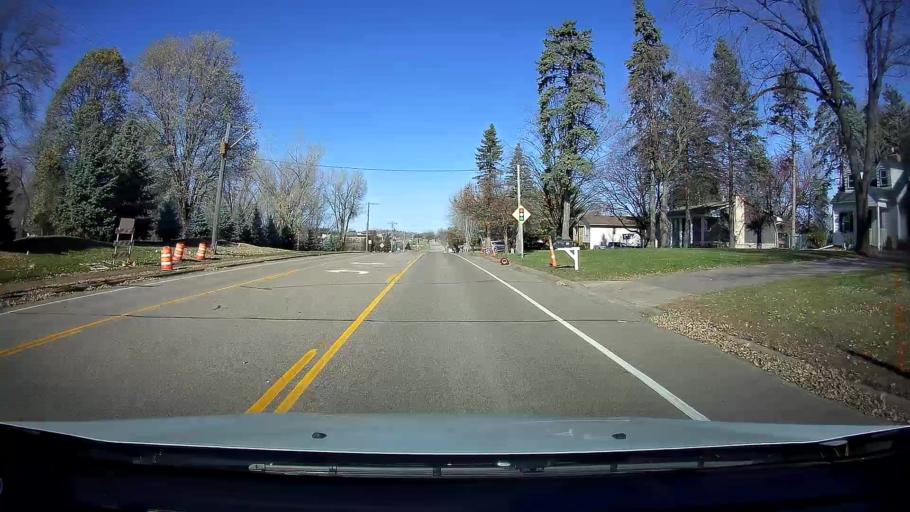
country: US
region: Minnesota
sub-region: Ramsey County
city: Shoreview
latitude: 45.0767
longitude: -93.1575
